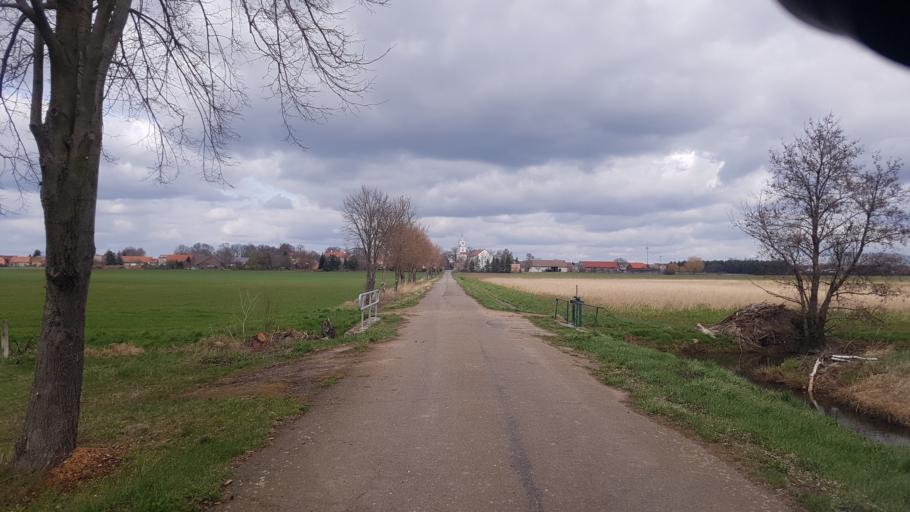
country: DE
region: Brandenburg
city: Hohenbucko
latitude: 51.6926
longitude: 13.4693
